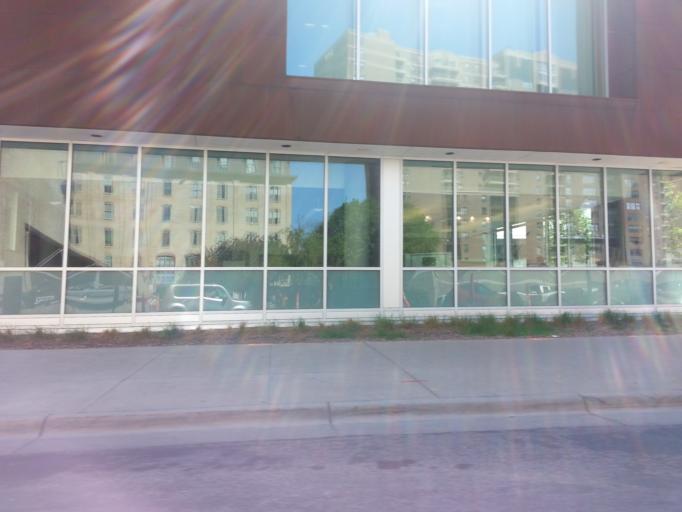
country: US
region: Minnesota
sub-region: Hennepin County
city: Minneapolis
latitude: 44.9797
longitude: -93.2602
